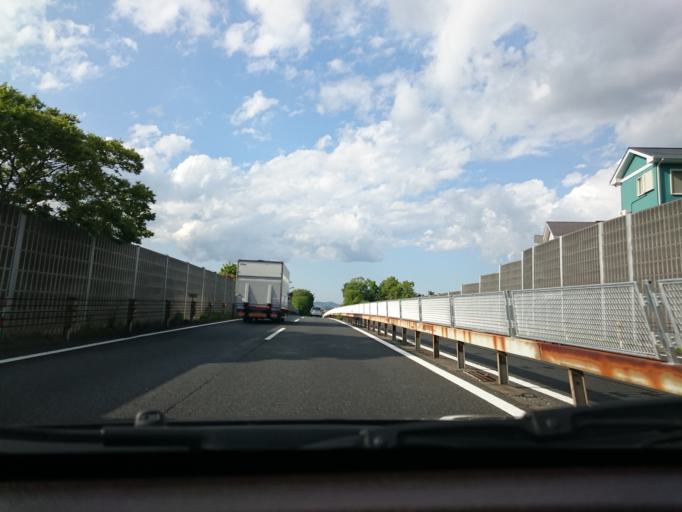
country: JP
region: Kanagawa
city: Oiso
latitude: 35.3427
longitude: 139.2966
